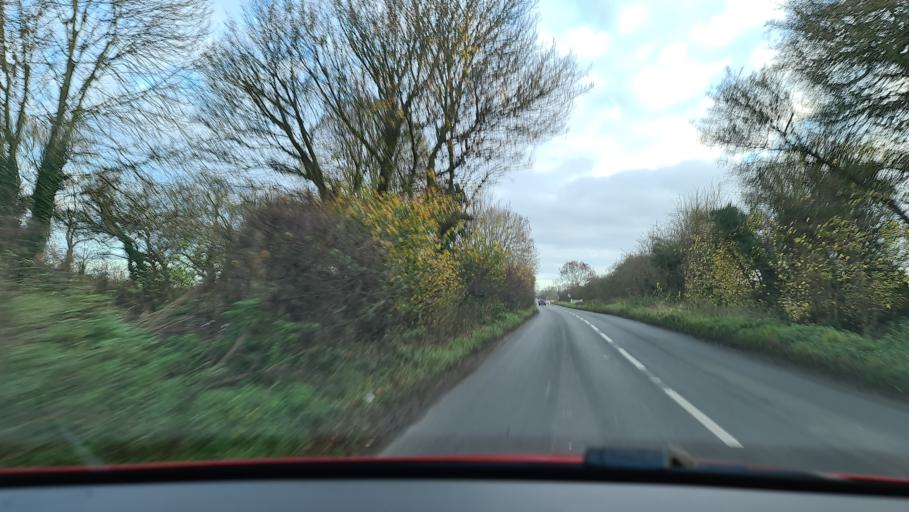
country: GB
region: England
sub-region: Buckinghamshire
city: Princes Risborough
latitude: 51.7222
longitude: -0.8716
